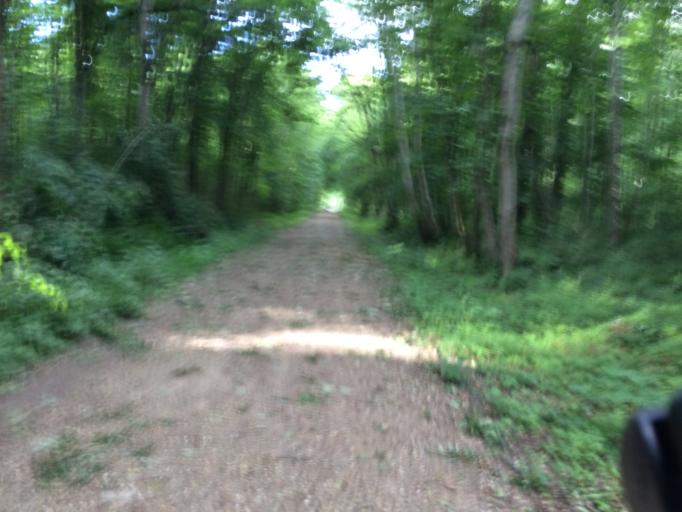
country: FR
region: Ile-de-France
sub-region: Departement de l'Essonne
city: Igny
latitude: 48.7573
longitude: 2.2432
